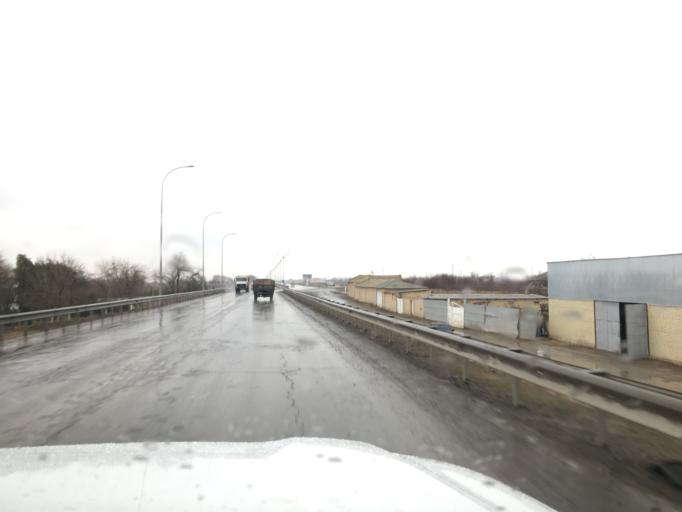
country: TM
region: Mary
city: Mary
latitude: 37.5514
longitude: 61.8622
